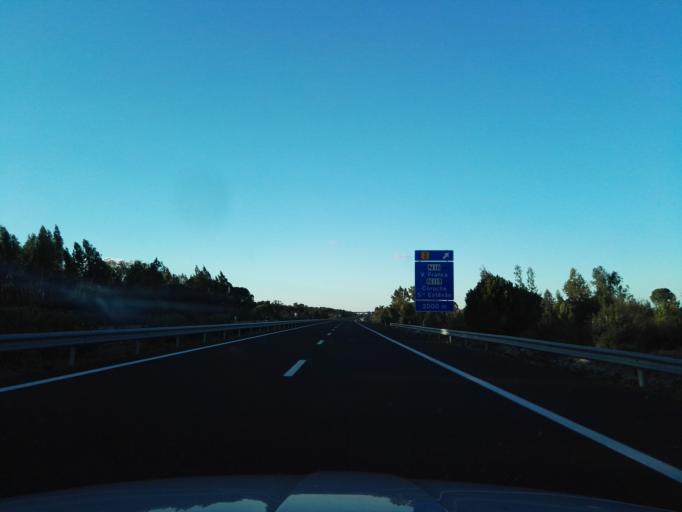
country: PT
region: Santarem
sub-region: Benavente
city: Poceirao
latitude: 38.8170
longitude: -8.7103
